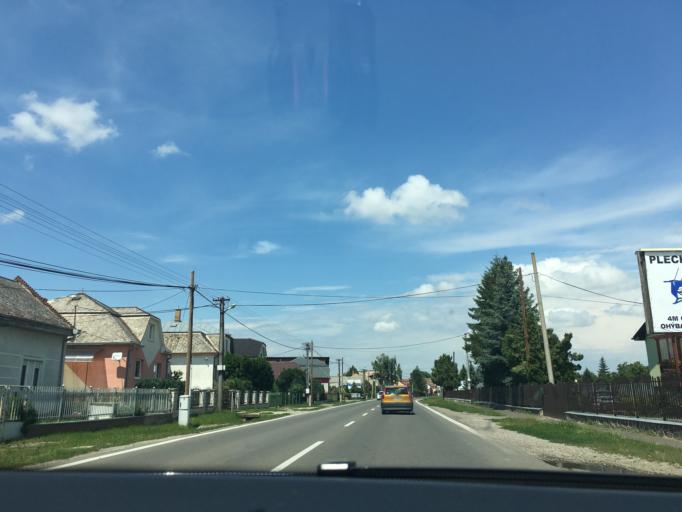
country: SK
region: Kosicky
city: Trebisov
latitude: 48.6648
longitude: 21.7117
